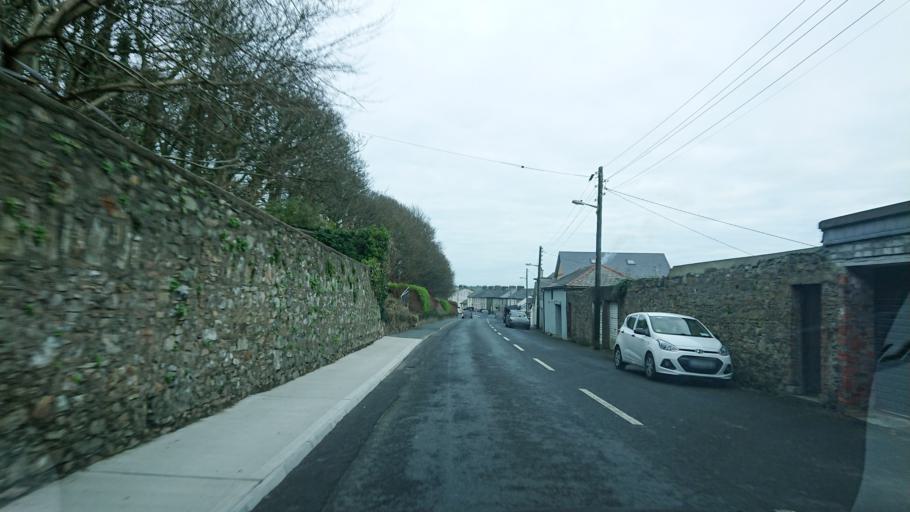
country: IE
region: Munster
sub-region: Waterford
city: Tra Mhor
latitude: 52.1638
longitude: -7.1485
